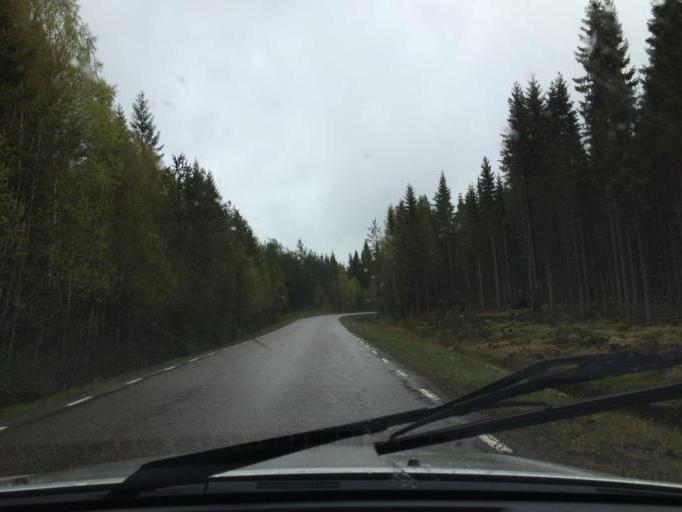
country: SE
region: Dalarna
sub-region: Ludvika Kommun
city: Abborrberget
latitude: 60.0660
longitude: 14.8254
